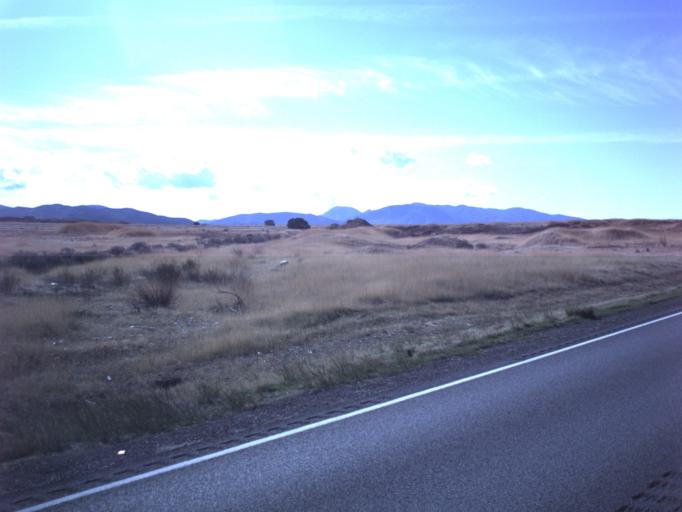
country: US
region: Utah
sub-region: Juab County
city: Nephi
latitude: 39.6604
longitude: -111.8546
